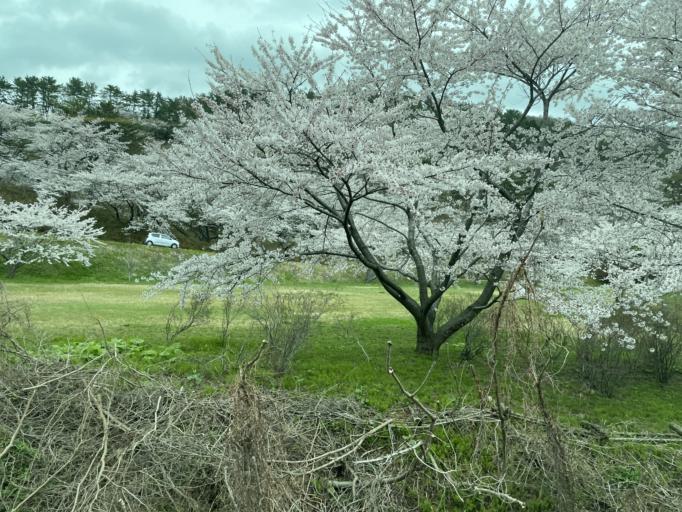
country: JP
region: Akita
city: Noshiromachi
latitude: 40.3893
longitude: 139.9837
